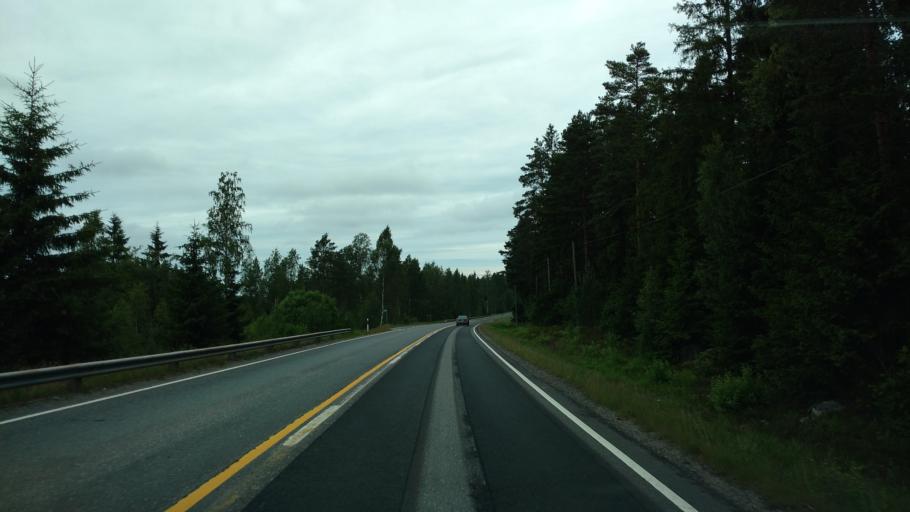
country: FI
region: Varsinais-Suomi
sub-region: Salo
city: Halikko
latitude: 60.4531
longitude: 23.0269
